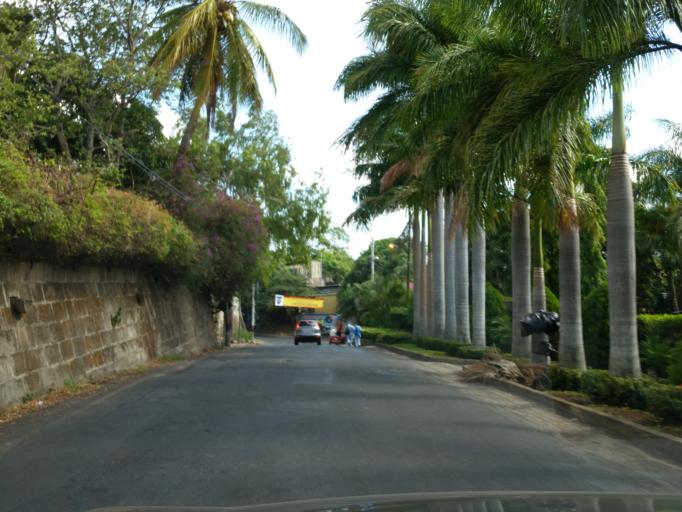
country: NI
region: Managua
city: Managua
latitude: 12.0835
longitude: -86.2393
